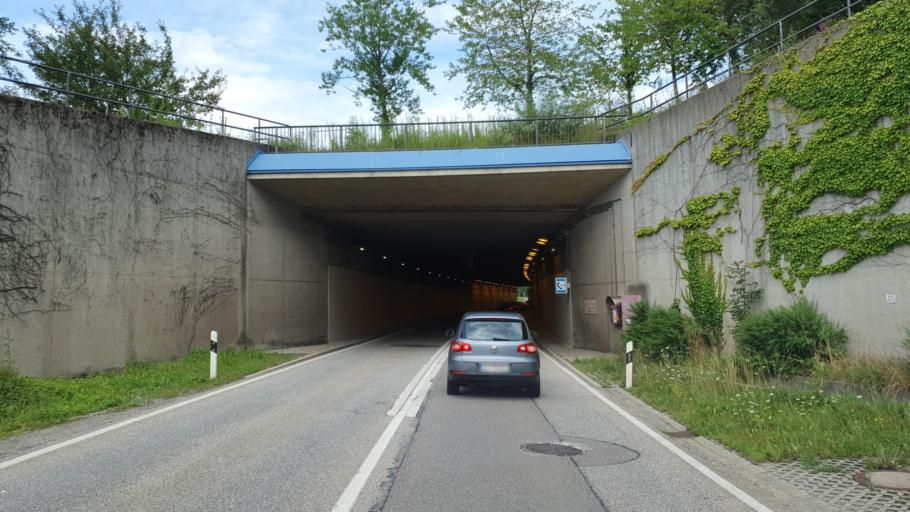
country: DE
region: Bavaria
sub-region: Swabia
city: Bodolz
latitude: 47.5764
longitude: 9.6889
